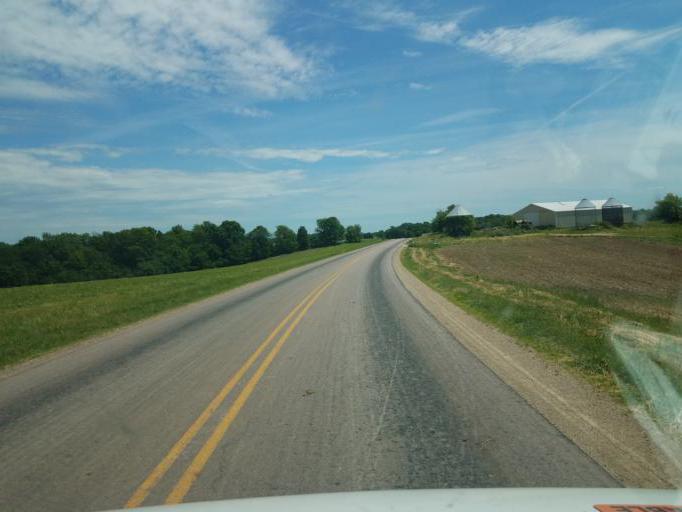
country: US
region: Wisconsin
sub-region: Vernon County
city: Hillsboro
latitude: 43.6033
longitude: -90.4238
